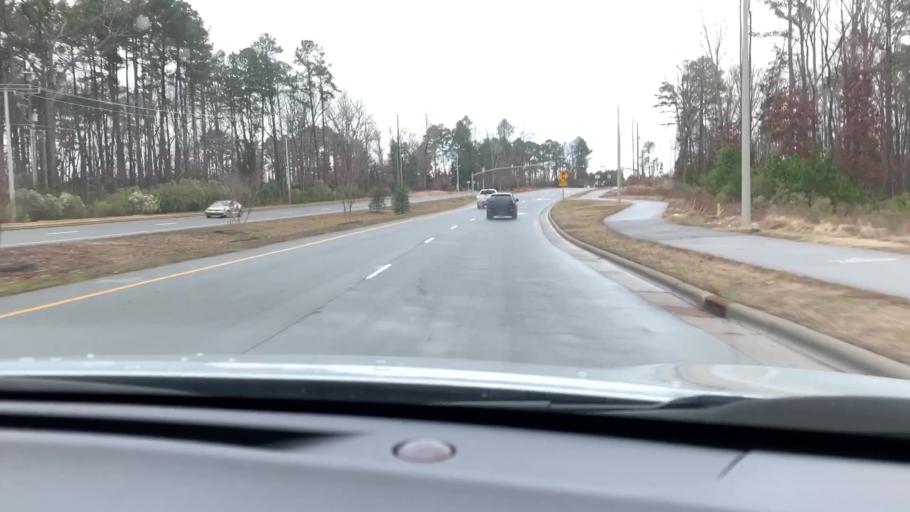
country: US
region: North Carolina
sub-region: Wake County
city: Green Level
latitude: 35.8273
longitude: -78.9011
